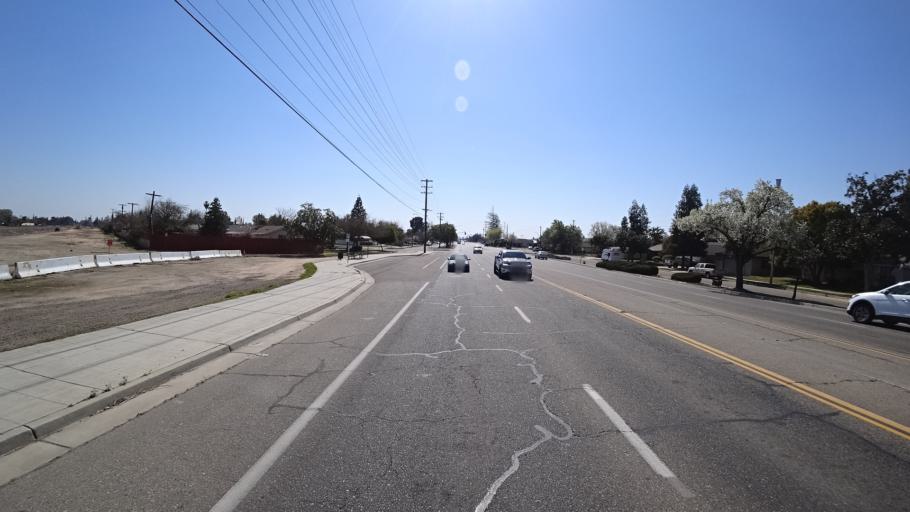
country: US
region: California
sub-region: Fresno County
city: Fresno
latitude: 36.7981
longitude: -119.8264
